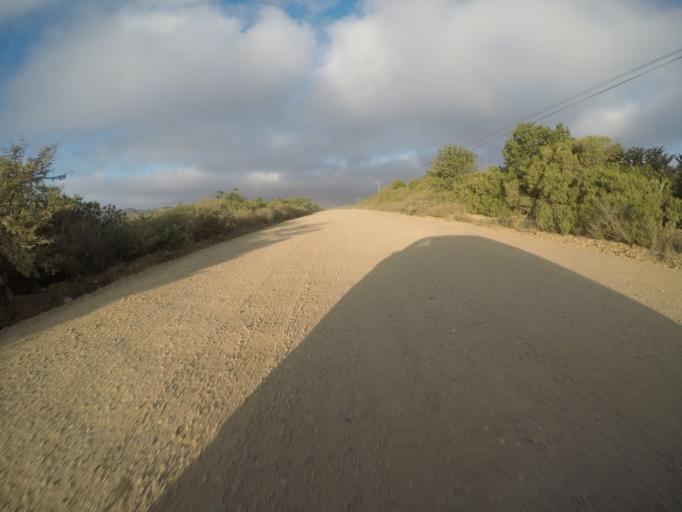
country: ZA
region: Western Cape
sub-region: Eden District Municipality
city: Mossel Bay
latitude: -34.1106
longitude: 22.0564
